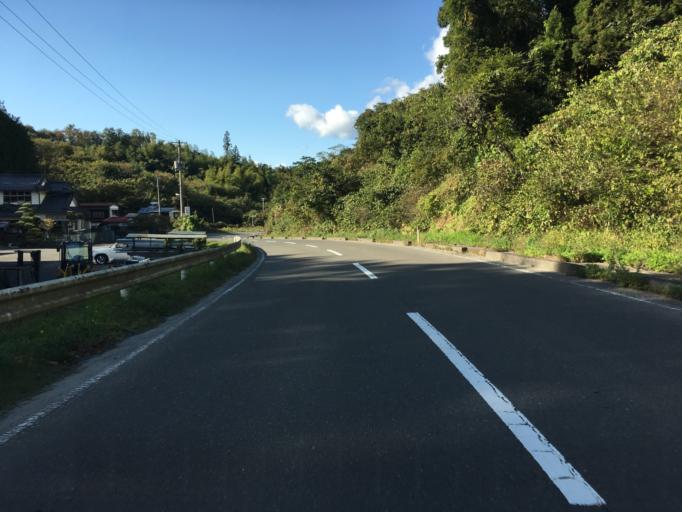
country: JP
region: Miyagi
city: Marumori
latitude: 37.8601
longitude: 140.8285
